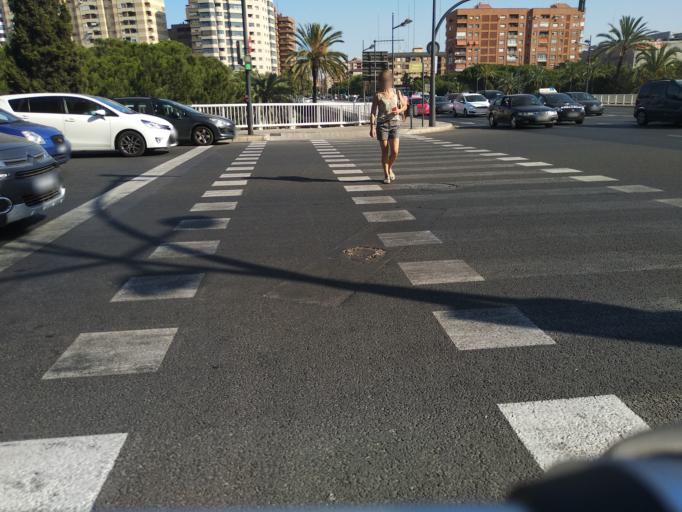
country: ES
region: Valencia
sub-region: Provincia de Valencia
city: Valencia
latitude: 39.4749
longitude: -0.3959
